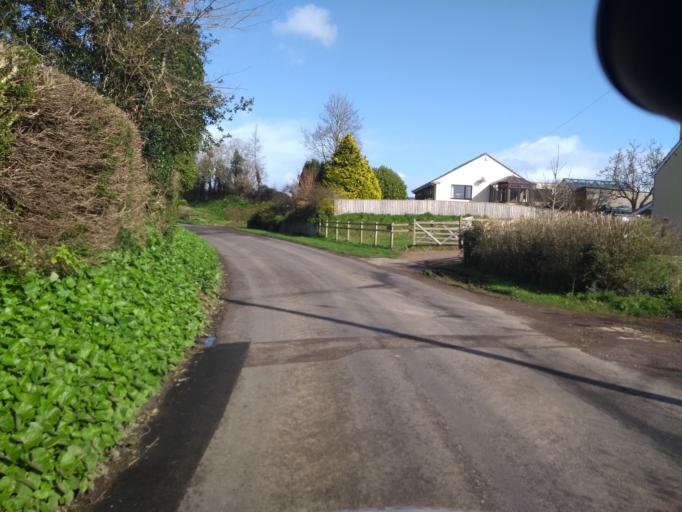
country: GB
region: England
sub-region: Somerset
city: South Petherton
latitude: 50.9650
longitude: -2.8345
